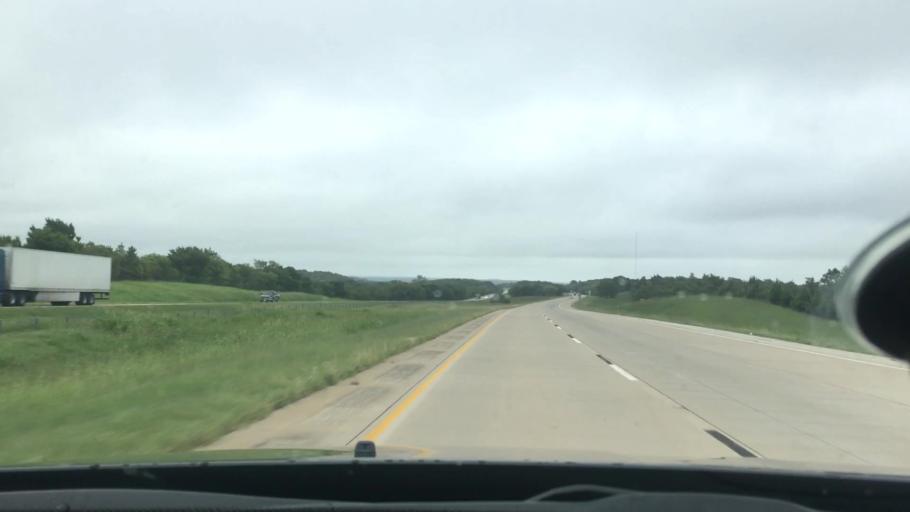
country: US
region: Oklahoma
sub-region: Okfuskee County
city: Okemah
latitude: 35.4300
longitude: -96.1883
